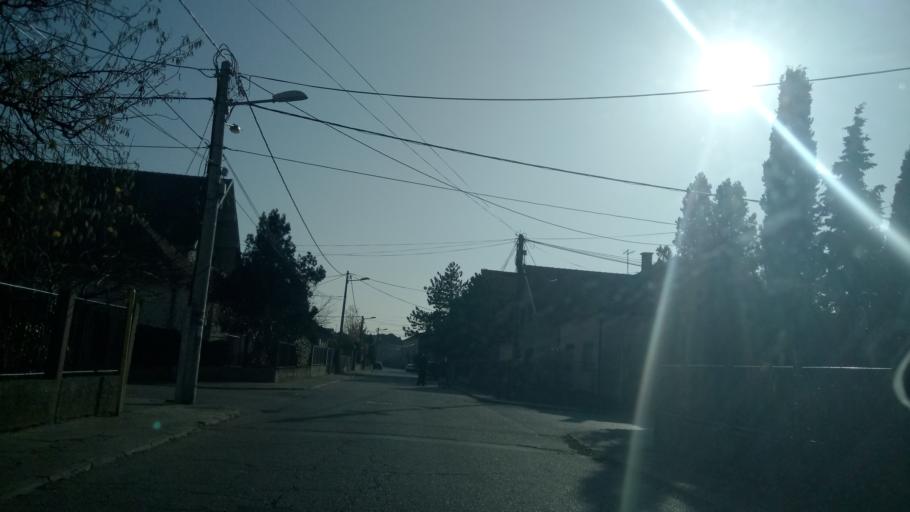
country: RS
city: Novi Banovci
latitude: 44.9038
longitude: 20.2875
